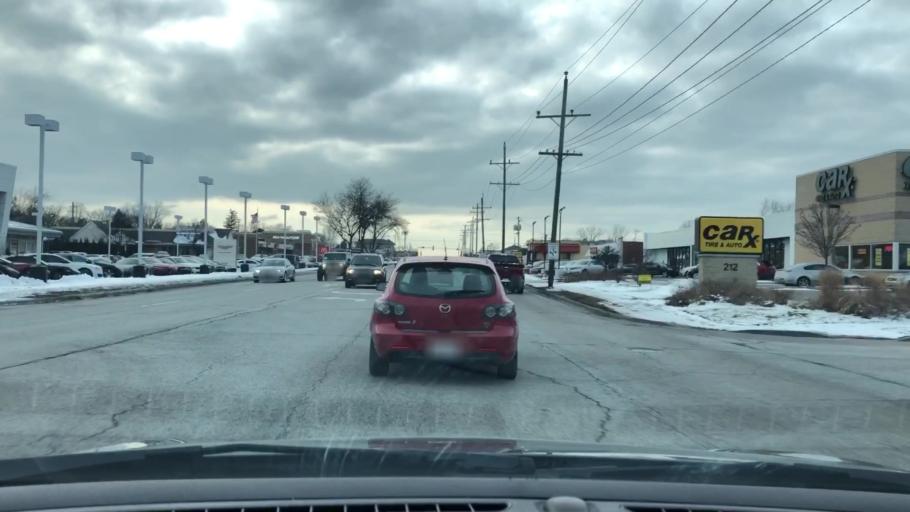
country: US
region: Illinois
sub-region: DuPage County
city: Westmont
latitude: 41.8097
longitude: -87.9904
